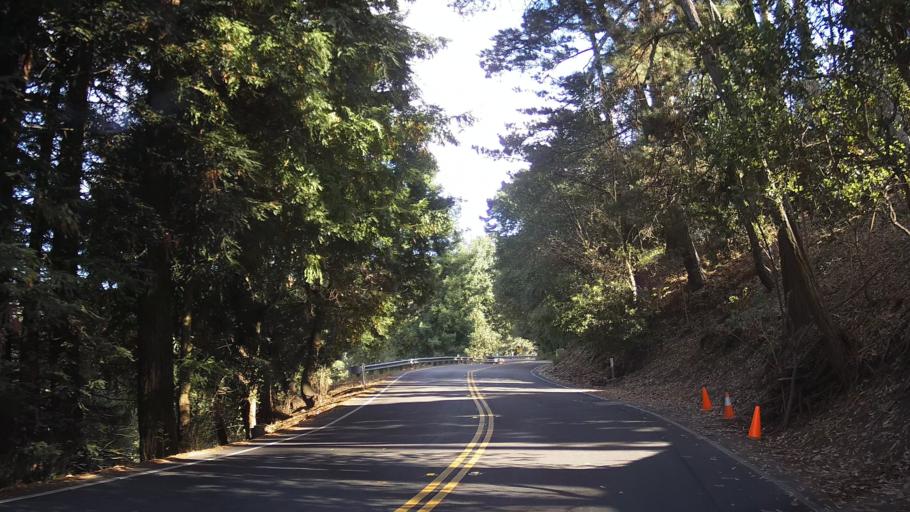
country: US
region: California
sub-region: Contra Costa County
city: Kensington
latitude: 37.8996
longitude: -122.2567
